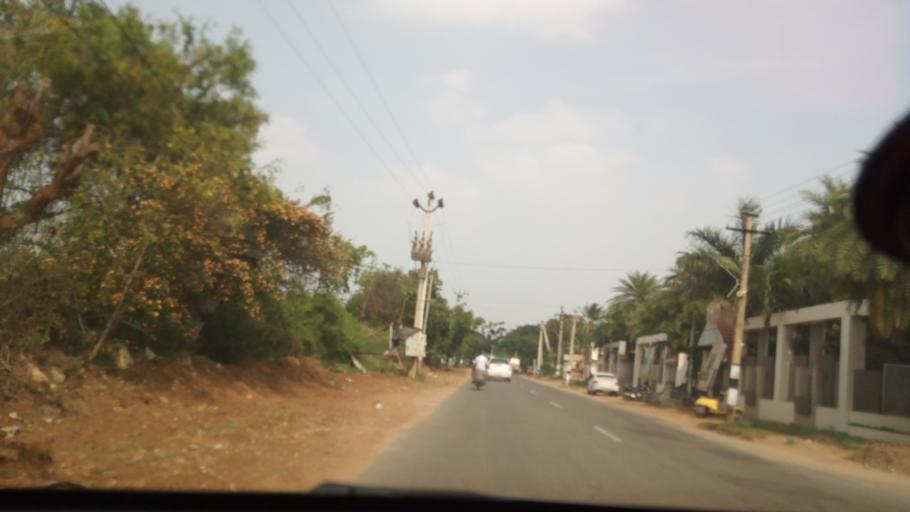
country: IN
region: Tamil Nadu
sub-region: Coimbatore
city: Perur
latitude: 11.0228
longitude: 76.8876
